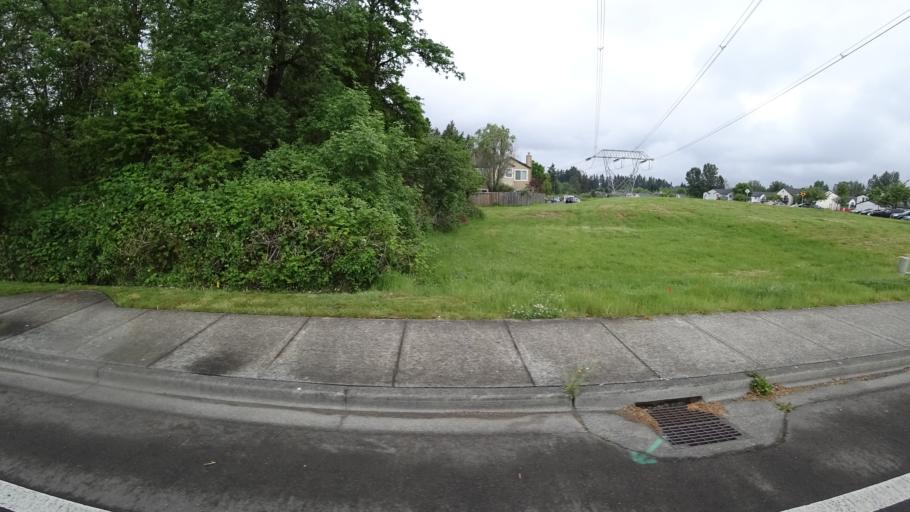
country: US
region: Oregon
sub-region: Washington County
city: Rockcreek
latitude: 45.5271
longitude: -122.8948
